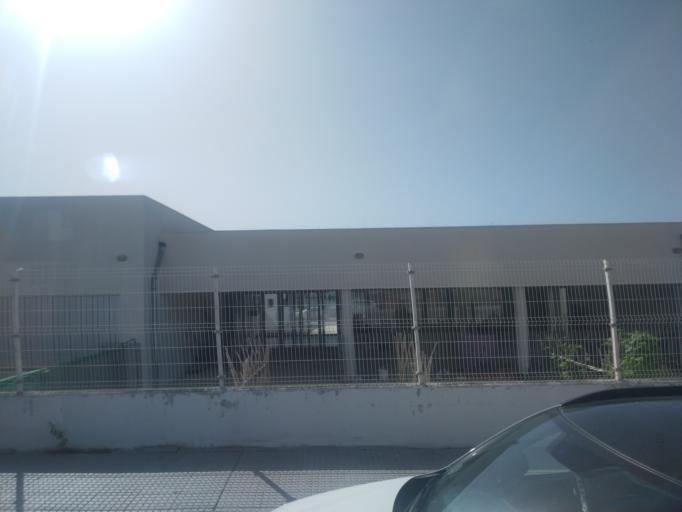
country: ES
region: Andalusia
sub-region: Provincia de Cadiz
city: San Fernando
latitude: 36.4497
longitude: -6.2170
